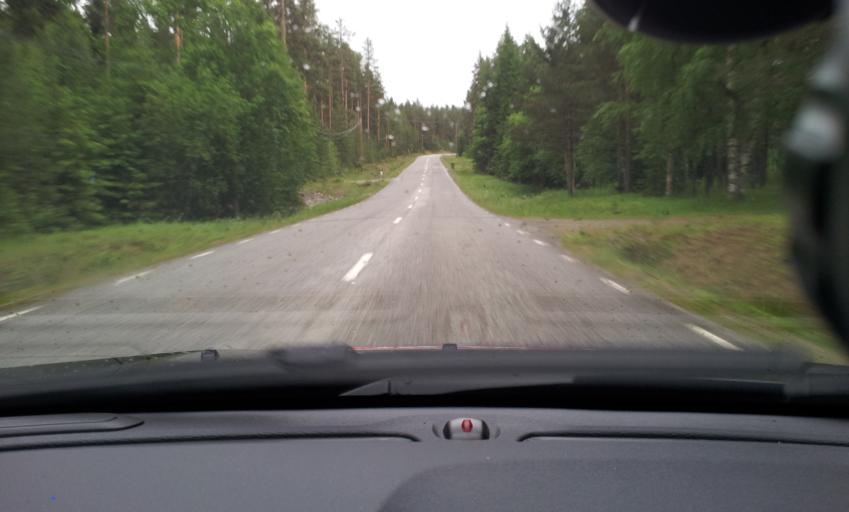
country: SE
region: Jaemtland
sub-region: Ragunda Kommun
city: Hammarstrand
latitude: 63.2524
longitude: 15.9050
